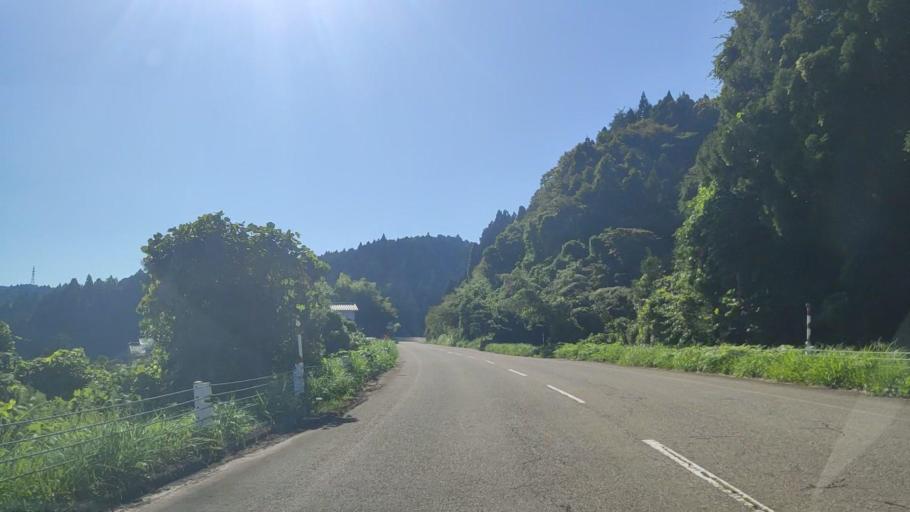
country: JP
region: Ishikawa
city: Nanao
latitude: 37.3151
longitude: 137.1505
